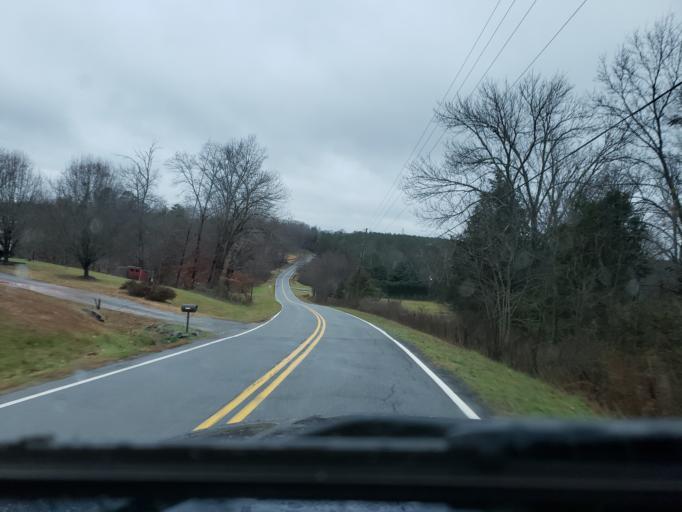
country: US
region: North Carolina
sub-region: Cleveland County
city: White Plains
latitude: 35.1809
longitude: -81.3712
